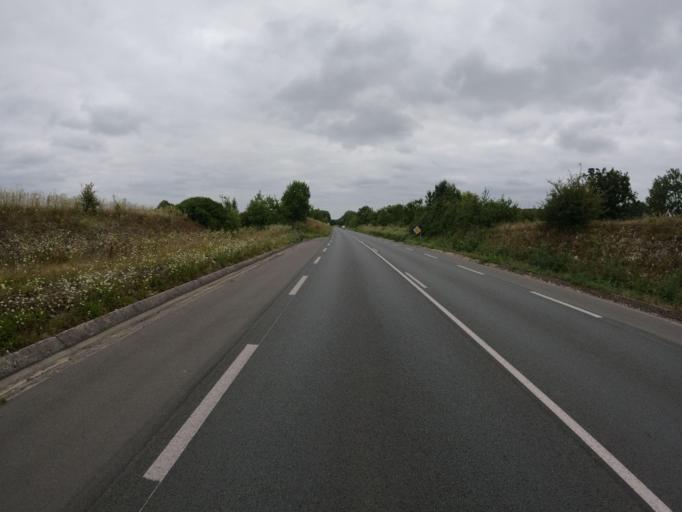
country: FR
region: Pays de la Loire
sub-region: Departement de la Vendee
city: Fontenay-le-Comte
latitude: 46.4624
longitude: -0.8431
